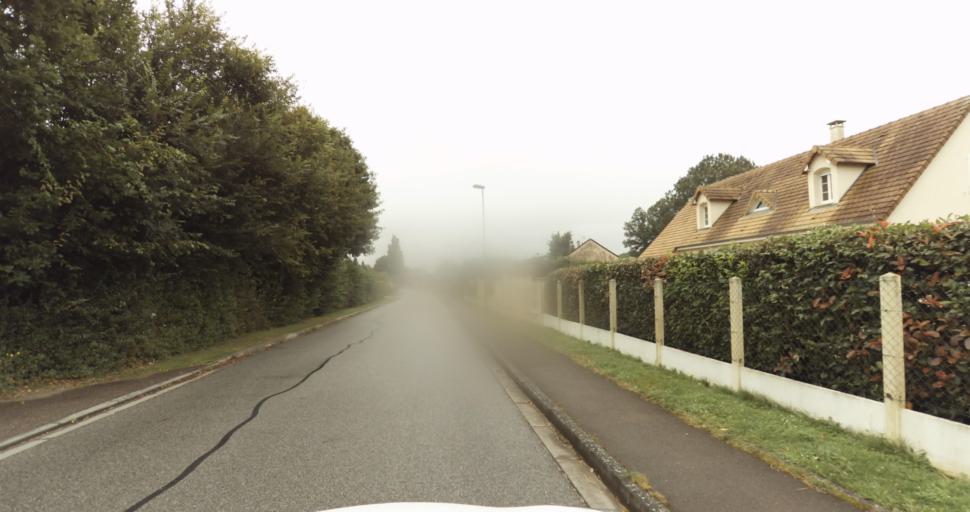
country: FR
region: Haute-Normandie
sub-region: Departement de l'Eure
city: Normanville
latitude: 49.0982
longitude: 1.1466
